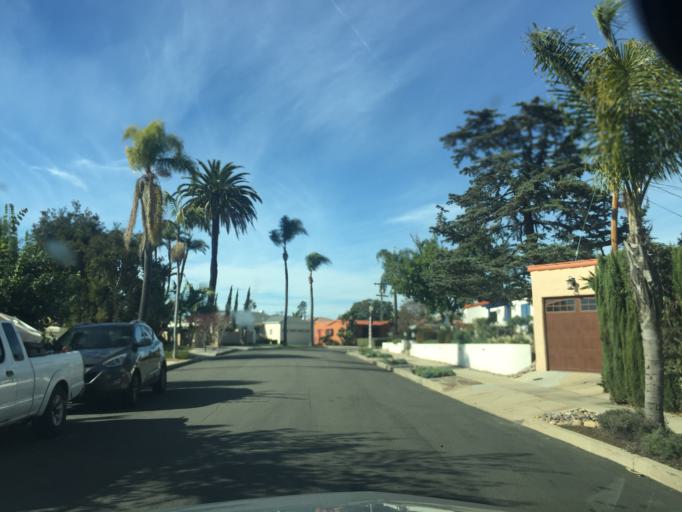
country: US
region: California
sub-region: San Diego County
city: Lemon Grove
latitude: 32.7697
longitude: -117.1024
